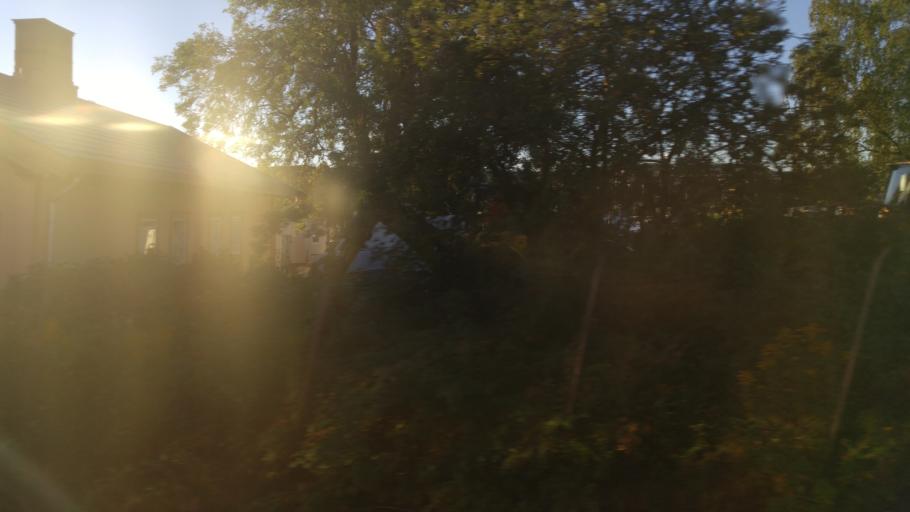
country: NO
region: Oslo
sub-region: Oslo
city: Oslo
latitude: 59.9369
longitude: 10.8405
